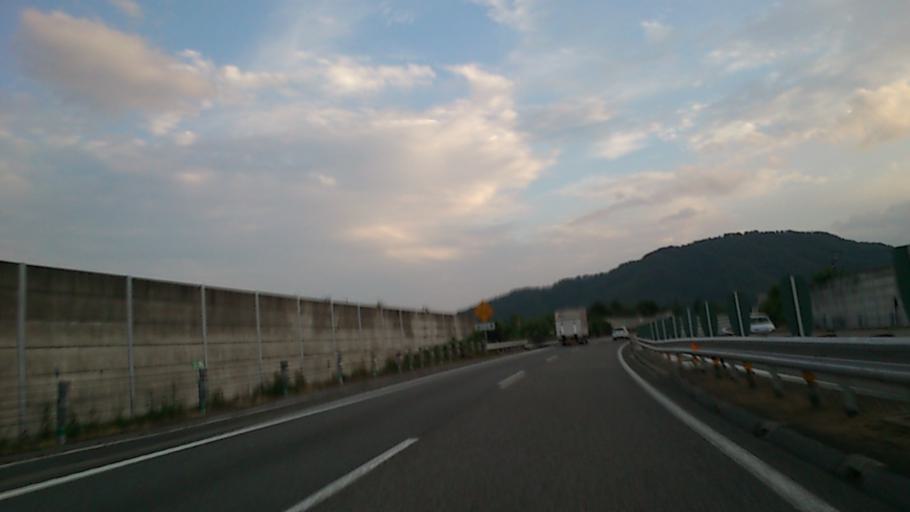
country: JP
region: Nagano
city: Iida
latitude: 35.4940
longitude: 137.7928
